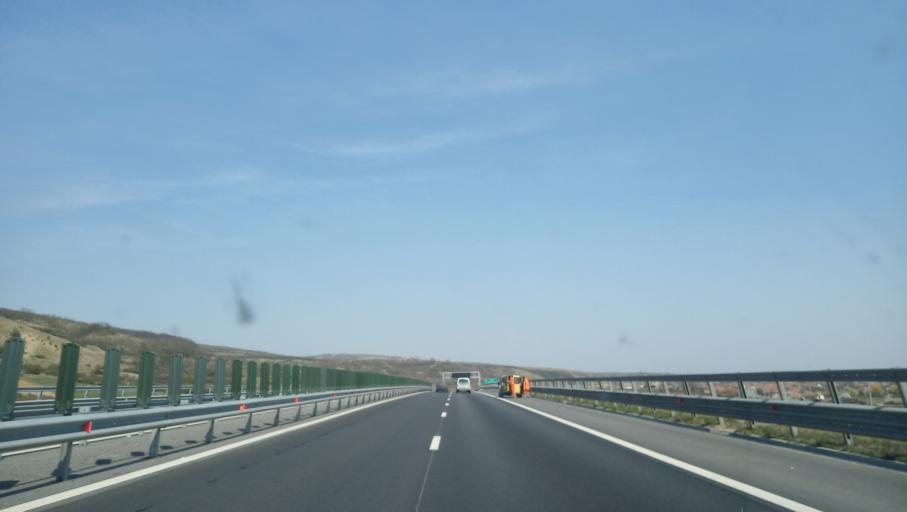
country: RO
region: Alba
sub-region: Comuna Miraslau
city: Miraslau
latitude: 46.3788
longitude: 23.7507
